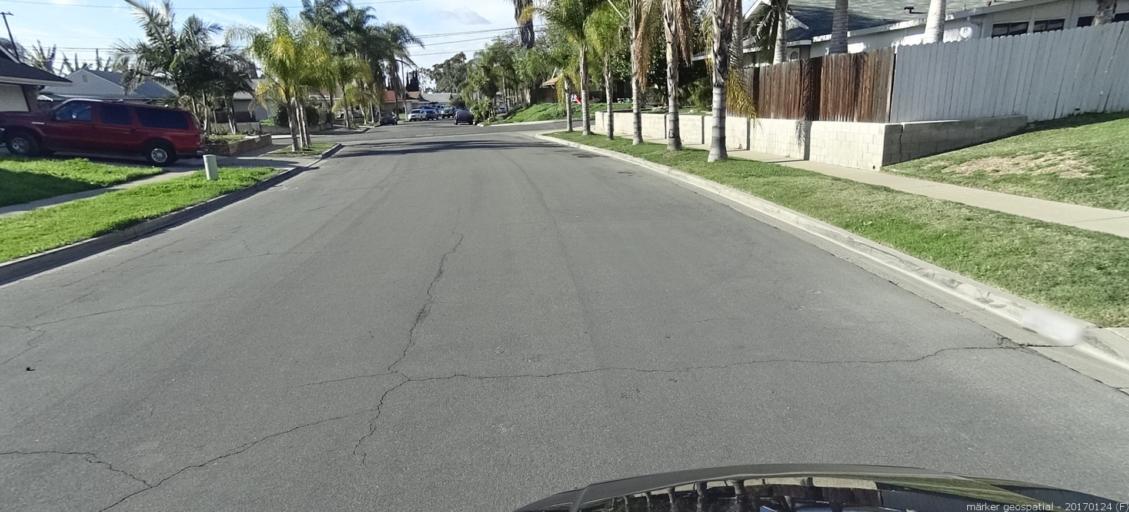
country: US
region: California
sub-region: Orange County
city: Laguna Hills
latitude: 33.6114
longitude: -117.7015
